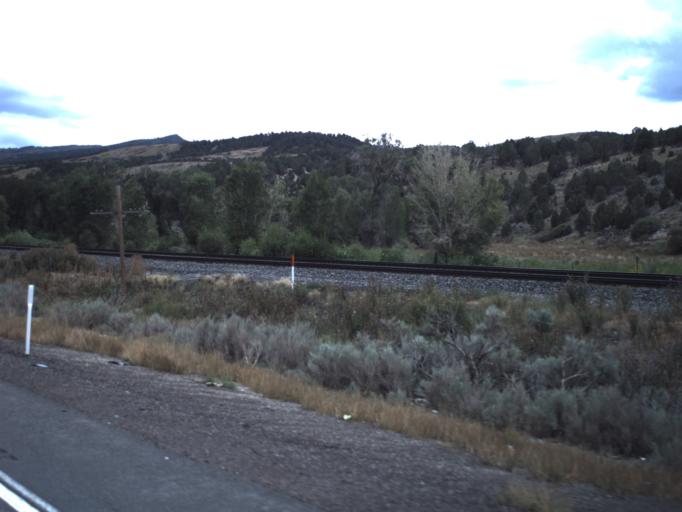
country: US
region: Utah
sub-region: Utah County
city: Mapleton
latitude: 39.9681
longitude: -111.3248
